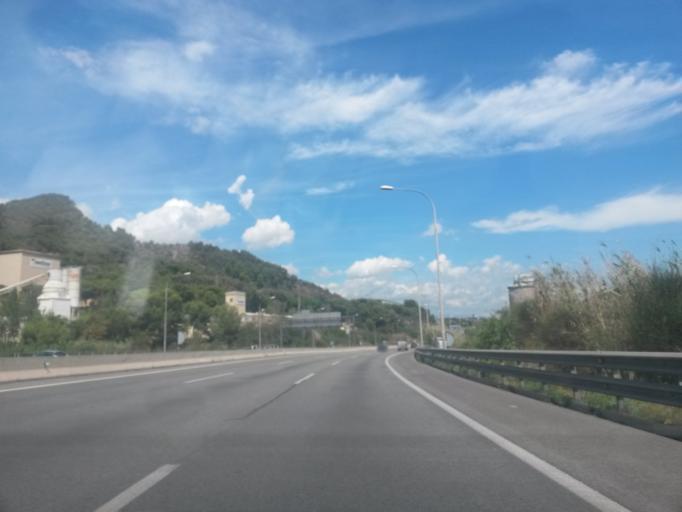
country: ES
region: Catalonia
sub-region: Provincia de Barcelona
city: Montcada i Reixac
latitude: 41.4696
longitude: 2.1778
